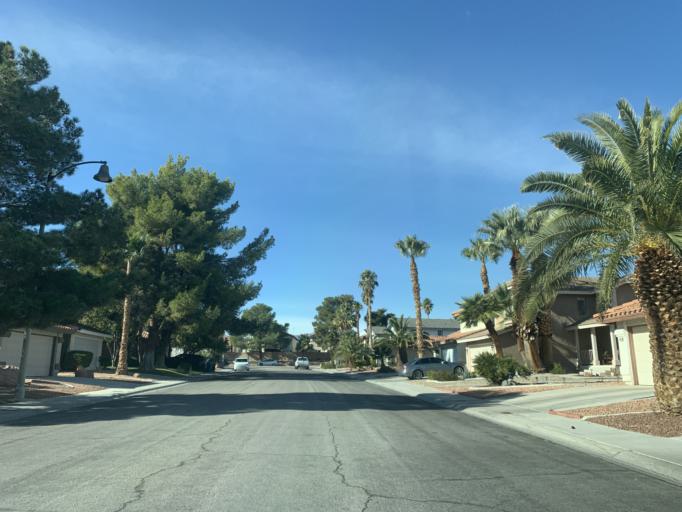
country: US
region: Nevada
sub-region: Clark County
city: Summerlin South
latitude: 36.1364
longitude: -115.2915
